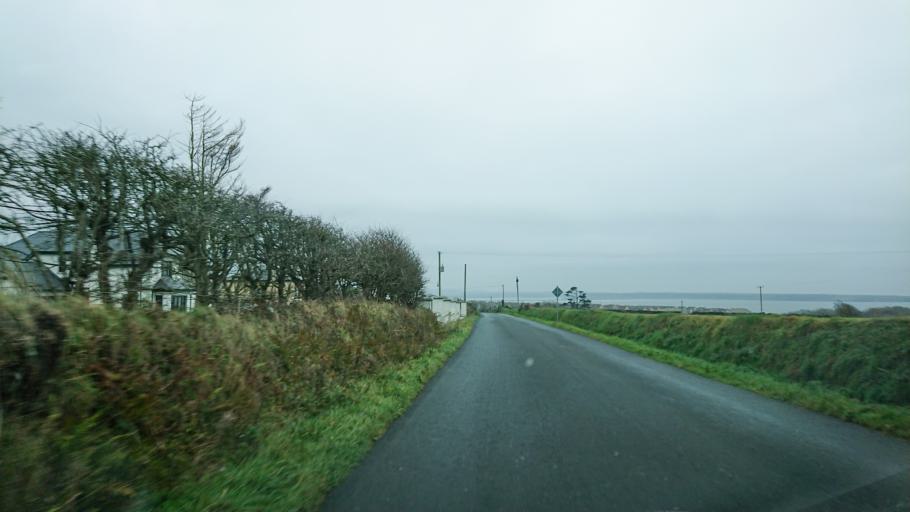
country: IE
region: Munster
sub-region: Waterford
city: Tra Mhor
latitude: 52.1460
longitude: -7.1797
